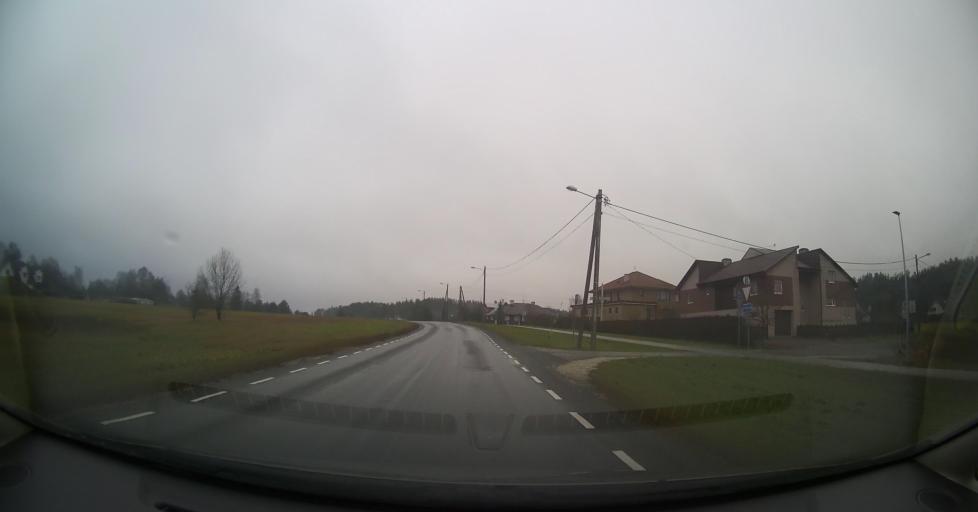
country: EE
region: Tartu
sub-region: Tartu linn
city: Tartu
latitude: 58.3631
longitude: 26.7975
